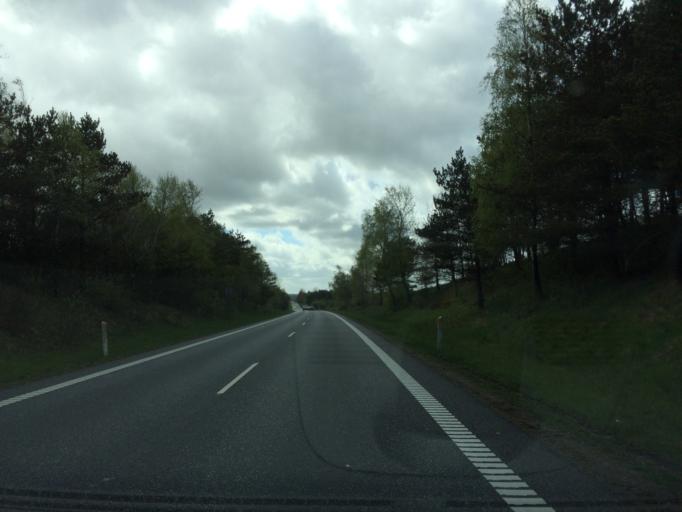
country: DK
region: Central Jutland
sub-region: Viborg Kommune
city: Stoholm
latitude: 56.4183
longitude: 9.0357
